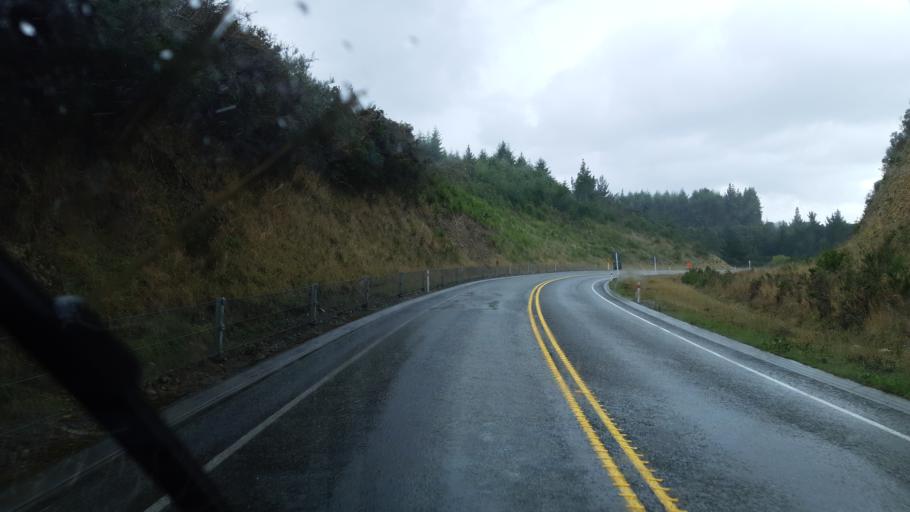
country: NZ
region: Tasman
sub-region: Tasman District
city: Wakefield
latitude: -41.4813
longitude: 172.9067
